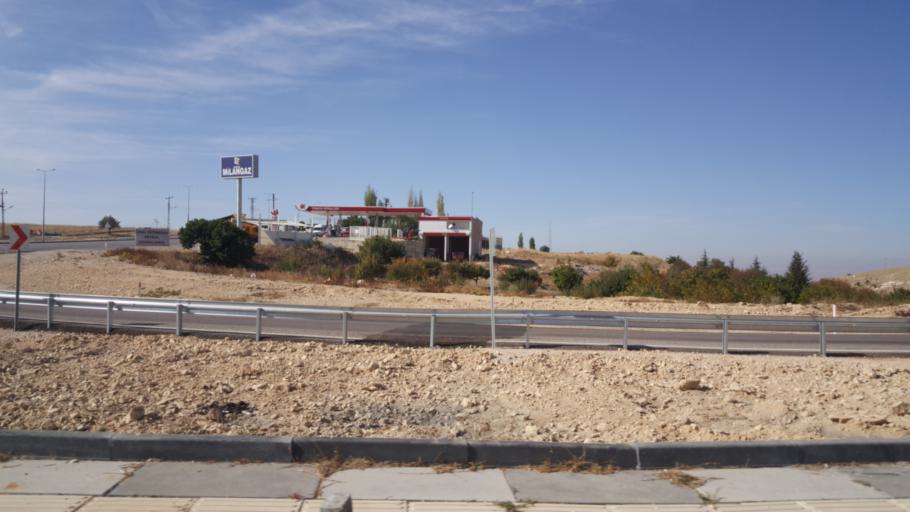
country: TR
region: Ankara
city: Haymana
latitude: 39.4307
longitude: 32.5217
